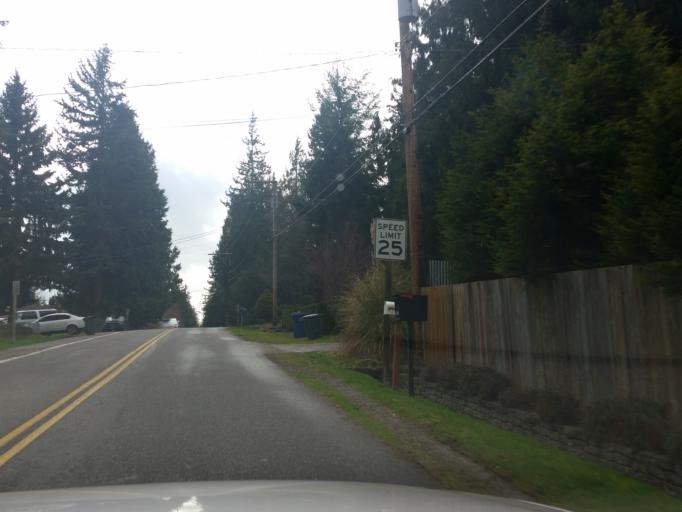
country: US
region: Washington
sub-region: Snohomish County
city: Meadowdale
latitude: 47.8574
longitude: -122.3096
